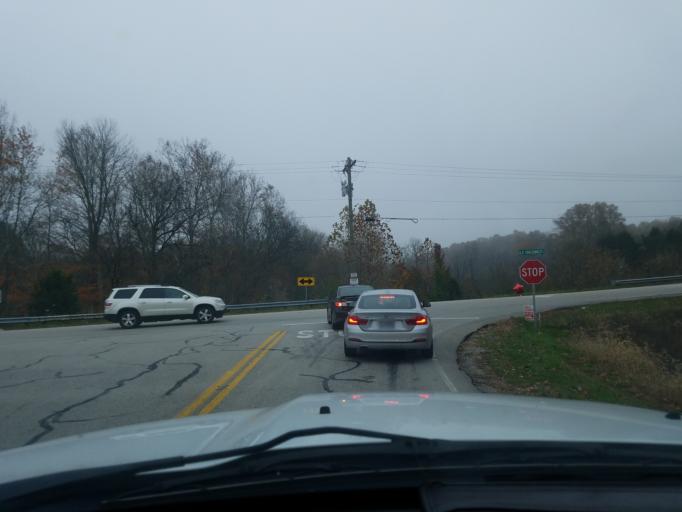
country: US
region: Indiana
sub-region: Floyd County
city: Galena
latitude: 38.3357
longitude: -85.9337
